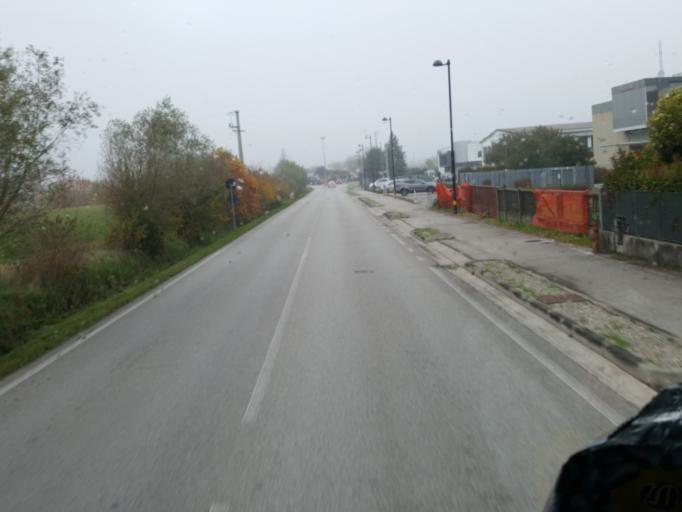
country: IT
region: Veneto
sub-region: Provincia di Padova
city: Campodarsego
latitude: 45.4827
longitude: 11.9037
